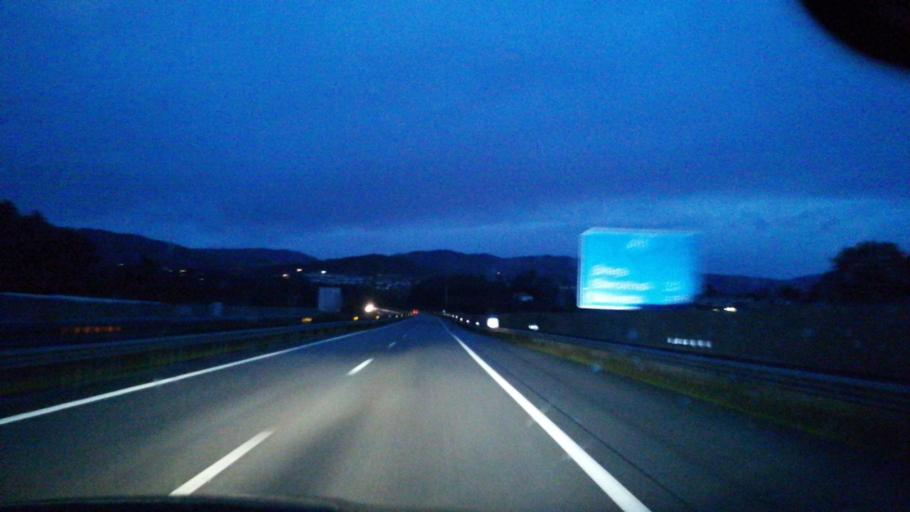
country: PT
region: Braga
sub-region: Guimaraes
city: Ponte
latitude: 41.4513
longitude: -8.3350
